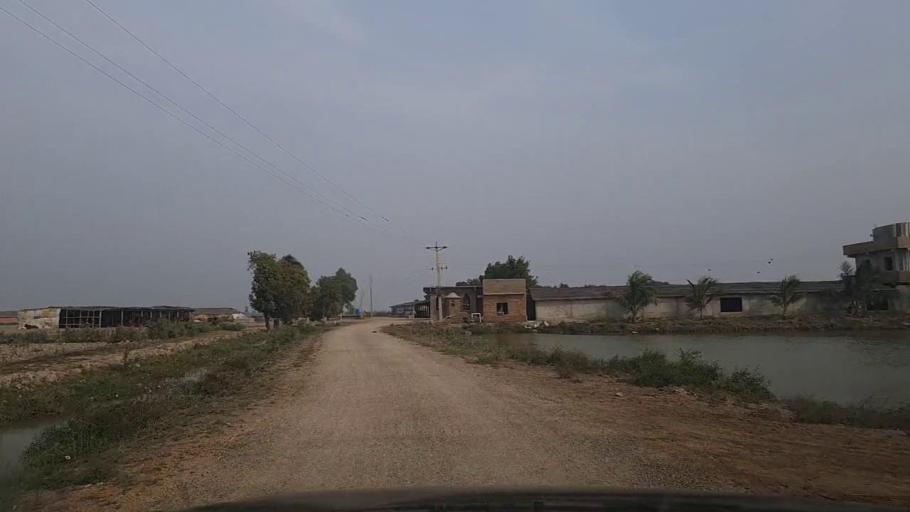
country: PK
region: Sindh
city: Chuhar Jamali
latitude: 24.5033
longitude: 67.8839
